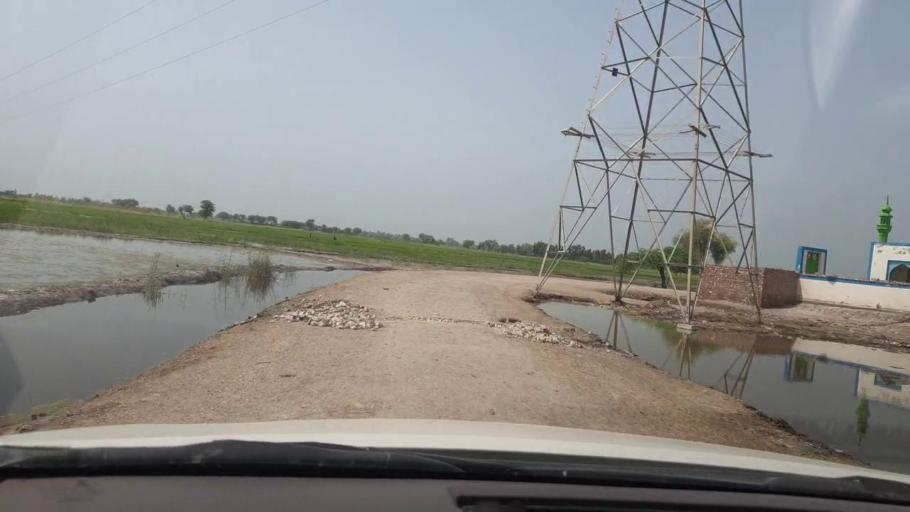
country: PK
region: Sindh
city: Shikarpur
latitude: 27.9983
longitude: 68.6250
